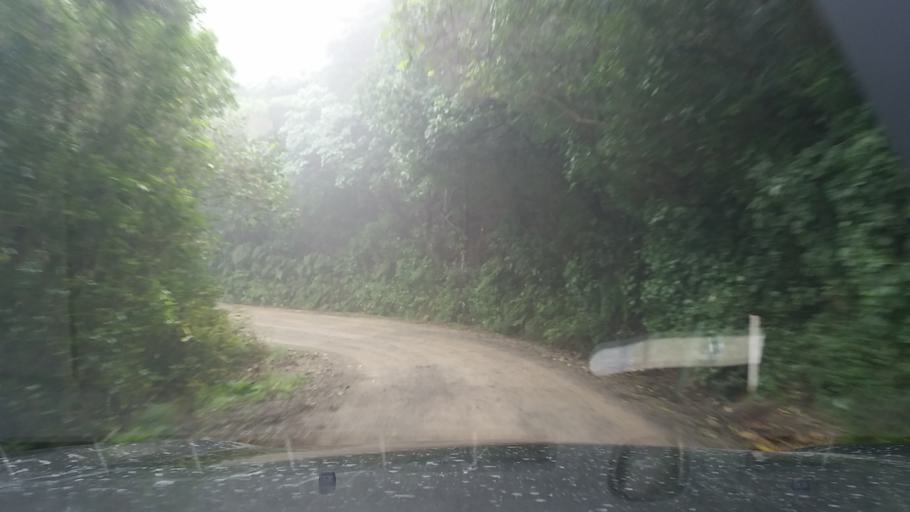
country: NZ
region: Marlborough
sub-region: Marlborough District
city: Picton
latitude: -41.1793
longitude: 173.9796
